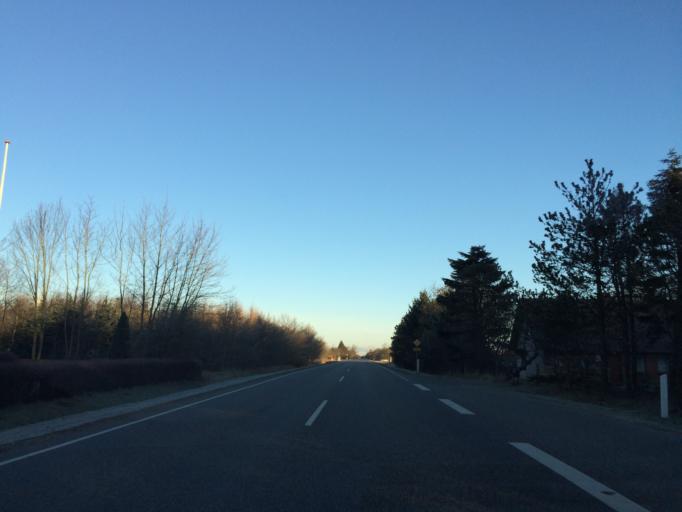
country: DK
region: Central Jutland
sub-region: Holstebro Kommune
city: Ulfborg
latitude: 56.3699
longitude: 8.3331
